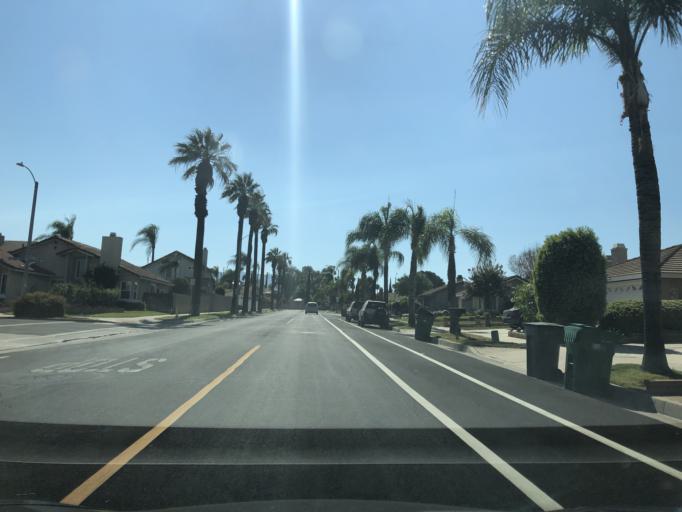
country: US
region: California
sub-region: Riverside County
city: Corona
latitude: 33.8540
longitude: -117.5515
